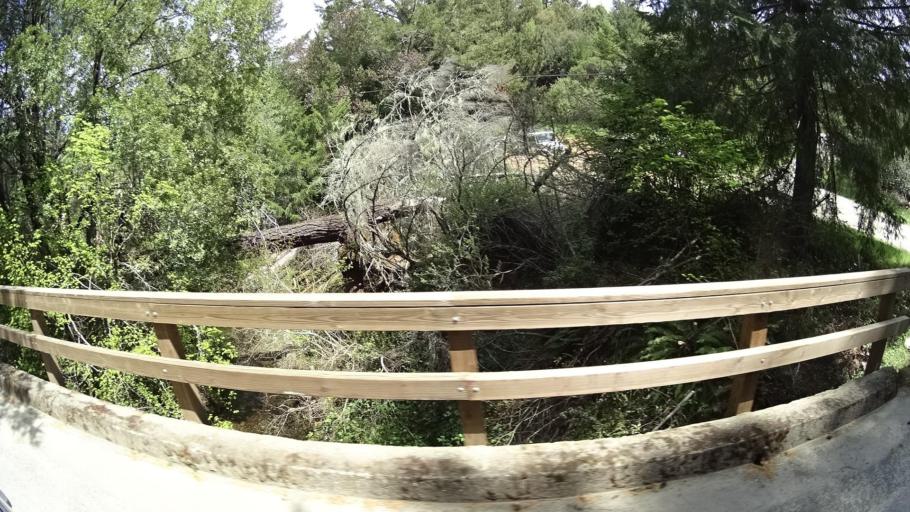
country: US
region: California
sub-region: Humboldt County
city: Redway
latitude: 40.0625
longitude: -123.9629
